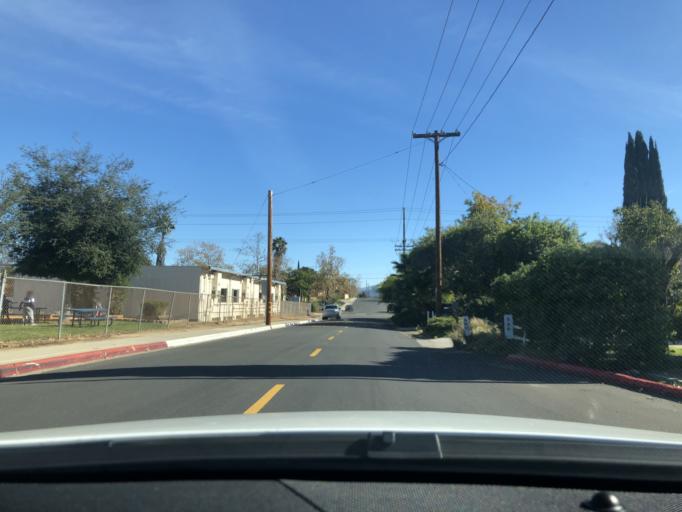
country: US
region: California
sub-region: San Diego County
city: Escondido
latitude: 33.0958
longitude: -117.0803
